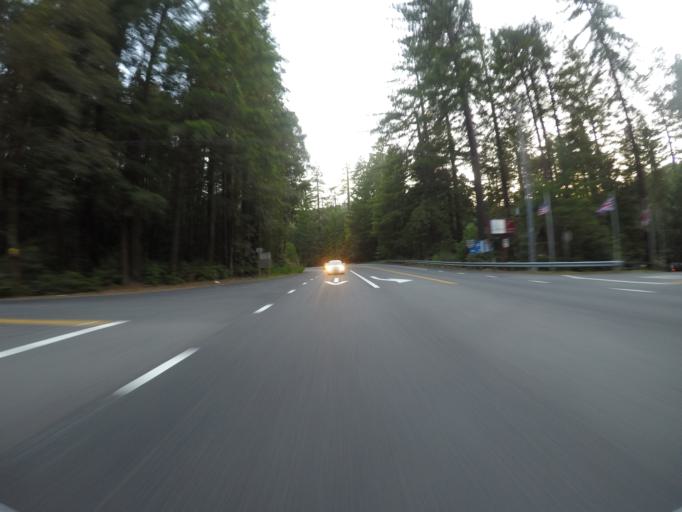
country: US
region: California
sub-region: Humboldt County
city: Redway
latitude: 39.9194
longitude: -123.7660
